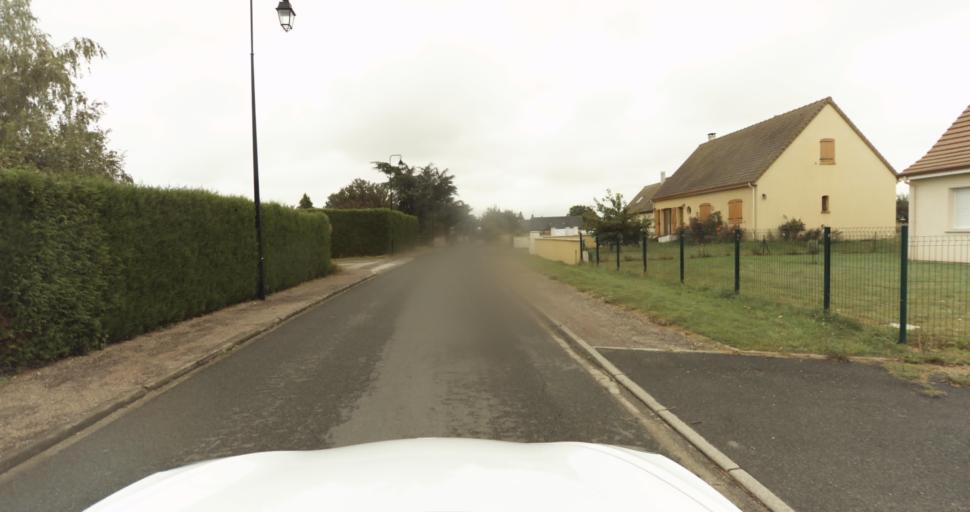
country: FR
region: Haute-Normandie
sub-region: Departement de l'Eure
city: Aviron
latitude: 49.0820
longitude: 1.0748
